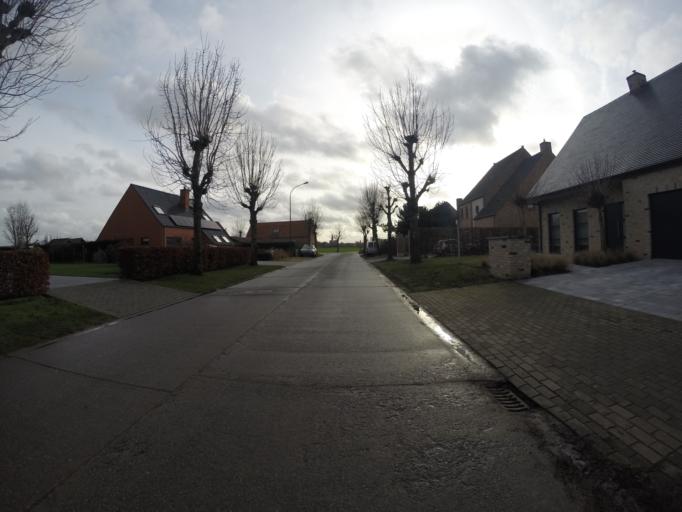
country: BE
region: Flanders
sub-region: Provincie Oost-Vlaanderen
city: Knesselare
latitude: 51.1499
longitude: 3.4099
